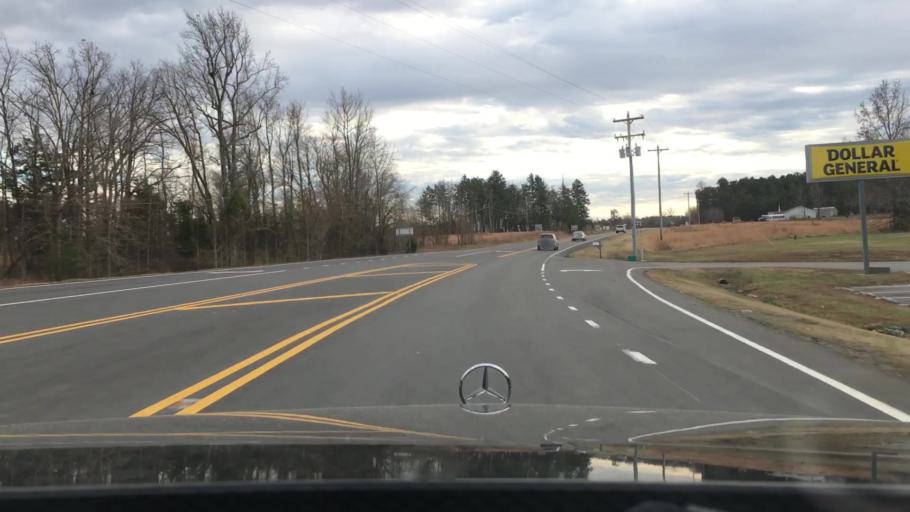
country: US
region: North Carolina
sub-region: Alamance County
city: Mebane
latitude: 36.2454
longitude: -79.1896
